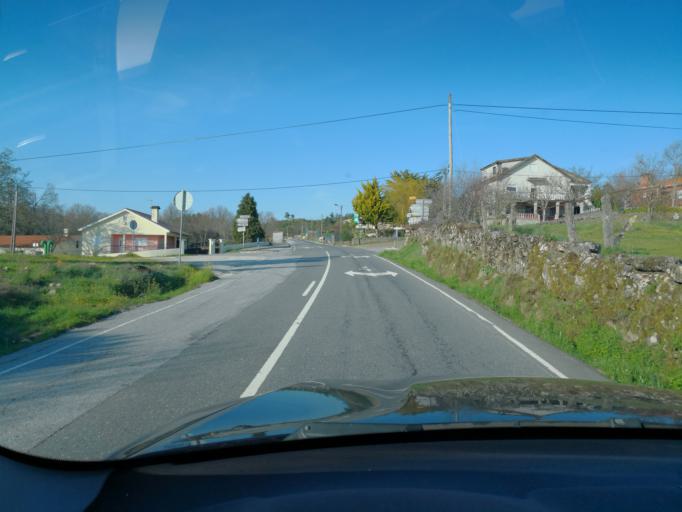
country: PT
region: Vila Real
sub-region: Vila Real
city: Vila Real
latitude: 41.3540
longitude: -7.6465
